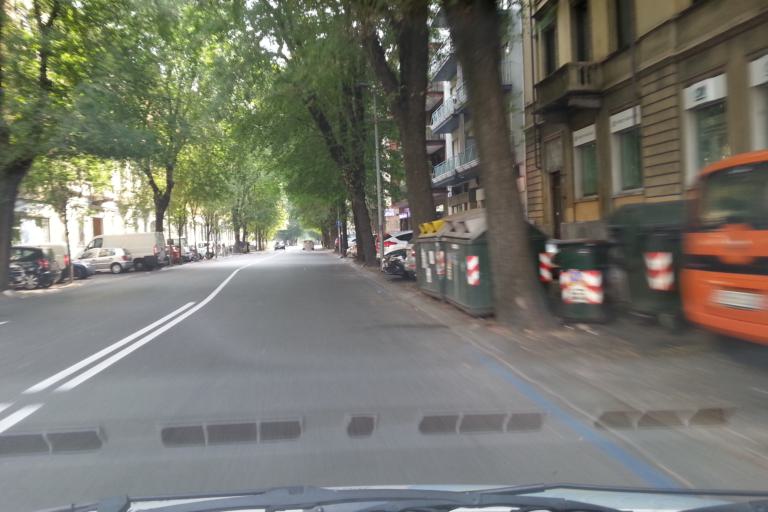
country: IT
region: Piedmont
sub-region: Provincia di Torino
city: Turin
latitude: 45.0474
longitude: 7.6735
